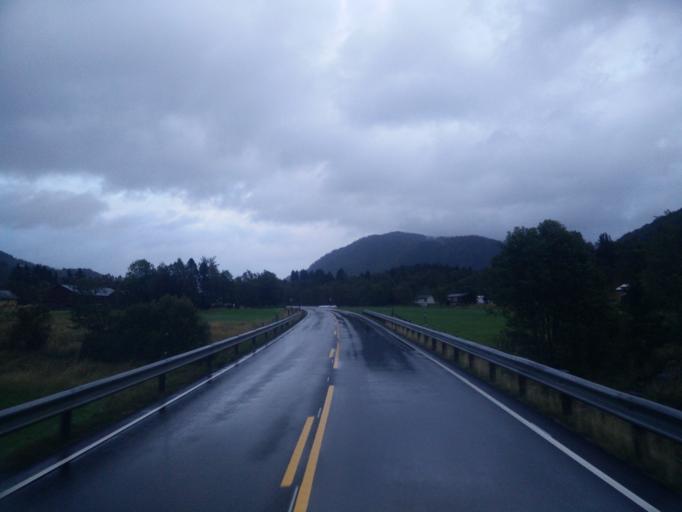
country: NO
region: More og Romsdal
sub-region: Rindal
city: Rindal
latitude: 63.0148
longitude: 9.0684
